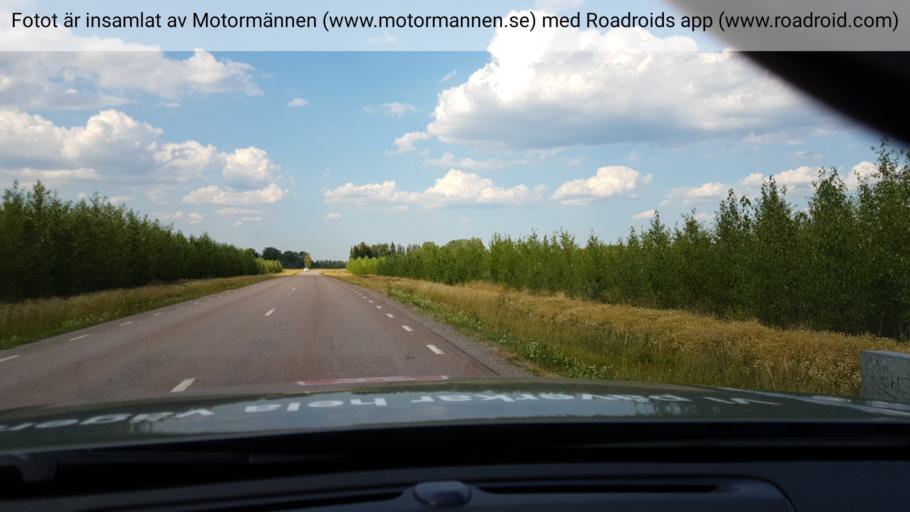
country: SE
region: Vaestmanland
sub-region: Vasteras
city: Tillberga
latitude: 59.6898
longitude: 16.6192
